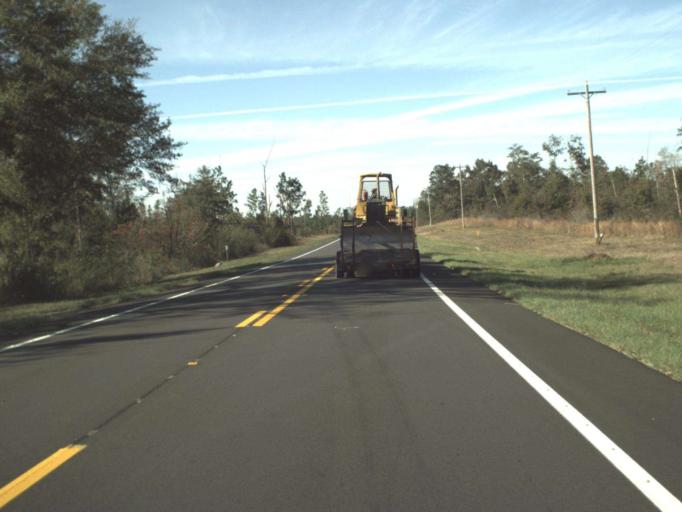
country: US
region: Alabama
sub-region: Escambia County
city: East Brewton
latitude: 30.9132
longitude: -87.0410
